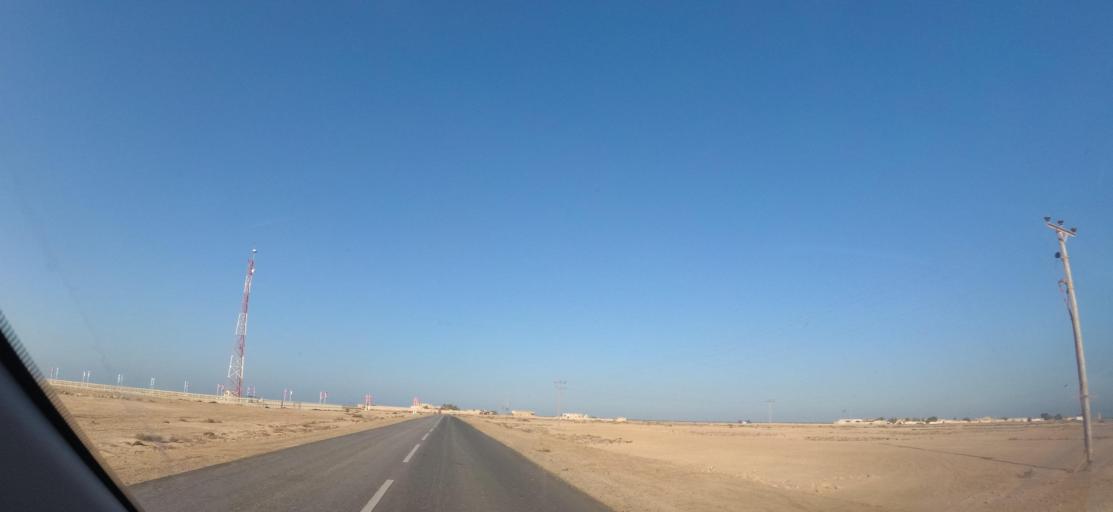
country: QA
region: Madinat ash Shamal
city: Ar Ru'ays
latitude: 26.1524
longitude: 51.2503
